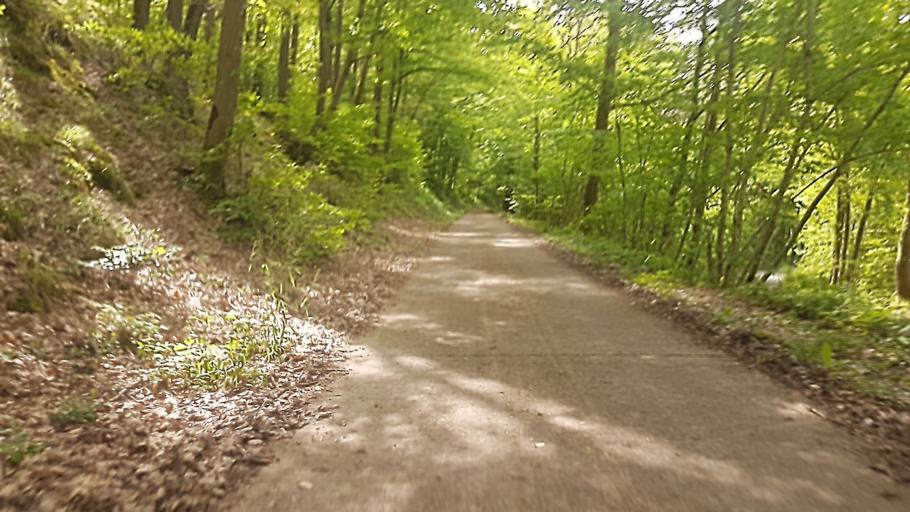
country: BE
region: Wallonia
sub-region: Province de Namur
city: Couvin
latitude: 50.0555
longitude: 4.5927
